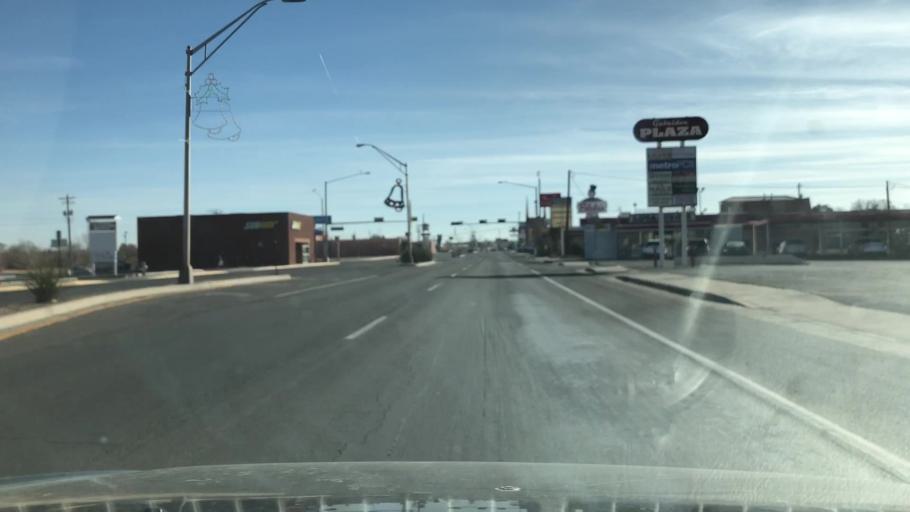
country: US
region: New Mexico
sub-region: Socorro County
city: Socorro
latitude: 34.0660
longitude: -106.8927
